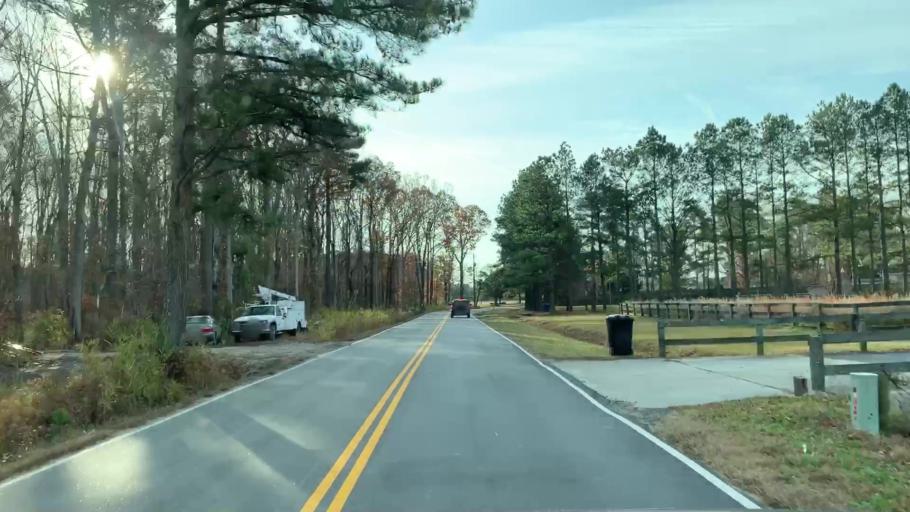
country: US
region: Virginia
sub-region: City of Virginia Beach
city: Virginia Beach
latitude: 36.7122
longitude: -76.0484
